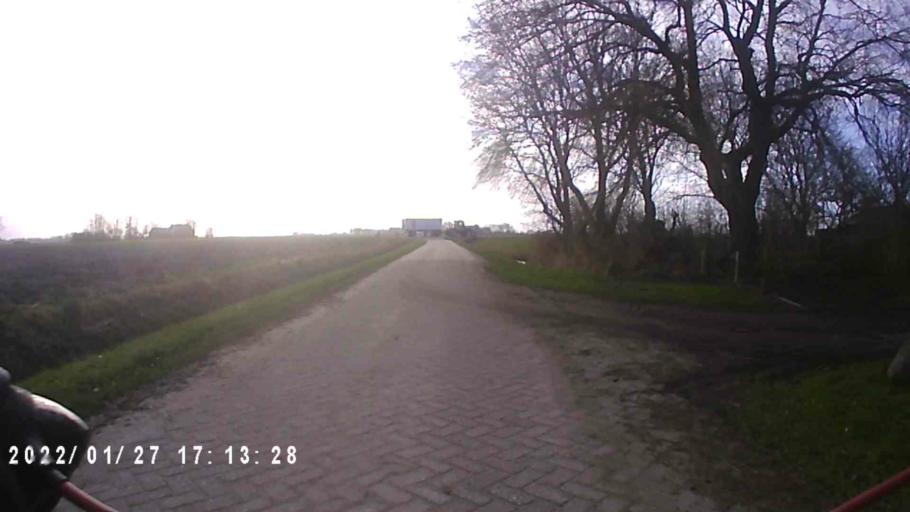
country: NL
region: Friesland
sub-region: Gemeente Dongeradeel
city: Anjum
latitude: 53.3971
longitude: 6.0917
